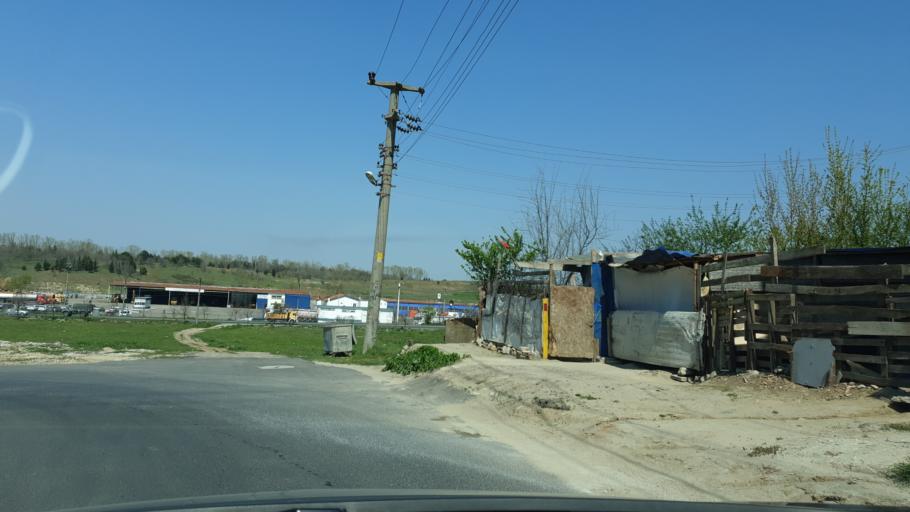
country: TR
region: Tekirdag
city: Corlu
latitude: 41.1668
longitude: 27.7904
